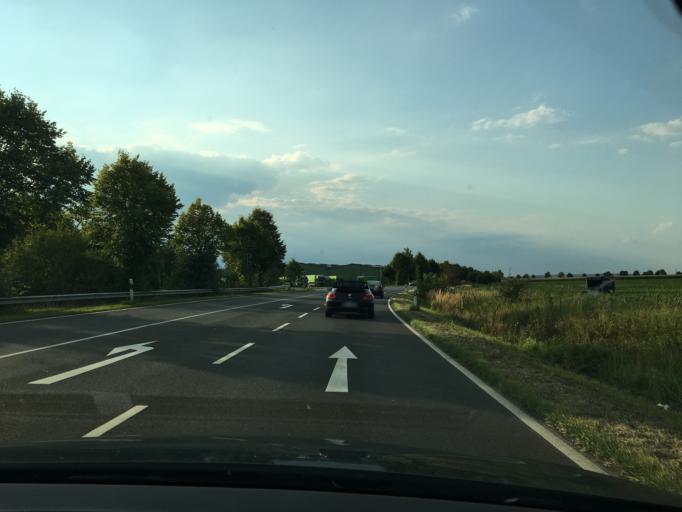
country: DE
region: North Rhine-Westphalia
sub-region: Regierungsbezirk Koln
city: Merzenich
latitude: 50.8167
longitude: 6.5494
